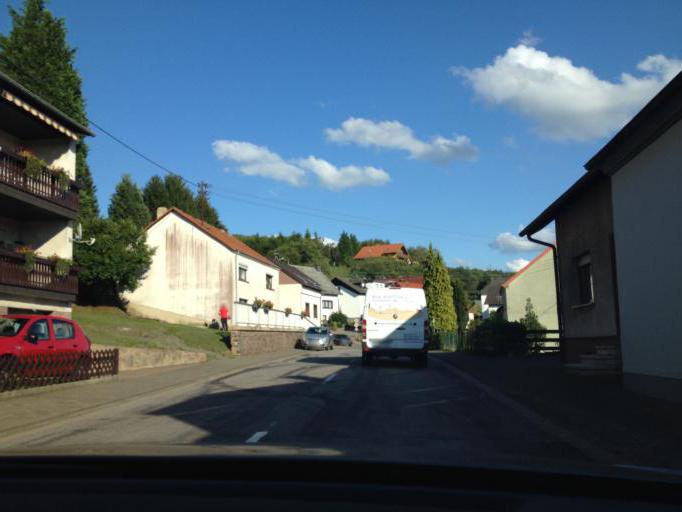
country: DE
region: Saarland
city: Wadern
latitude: 49.4845
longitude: 6.9445
